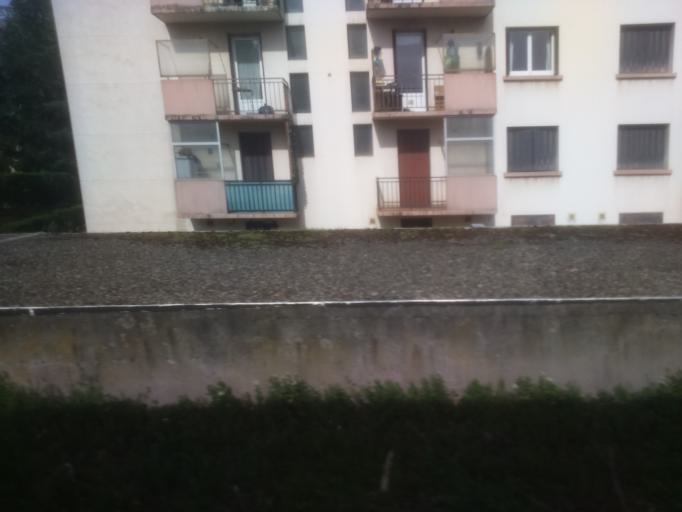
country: FR
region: Rhone-Alpes
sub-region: Departement de l'Isere
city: Le Pont-de-Claix
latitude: 45.1420
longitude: 5.7043
